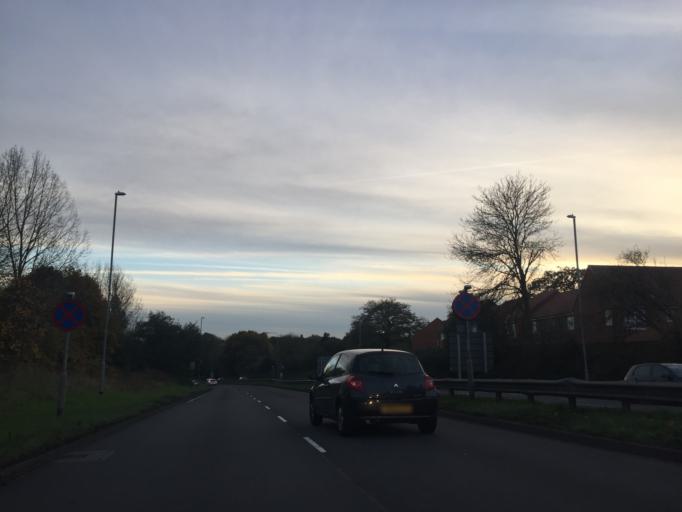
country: GB
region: England
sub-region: Northamptonshire
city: Northampton
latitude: 52.2754
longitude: -0.8459
